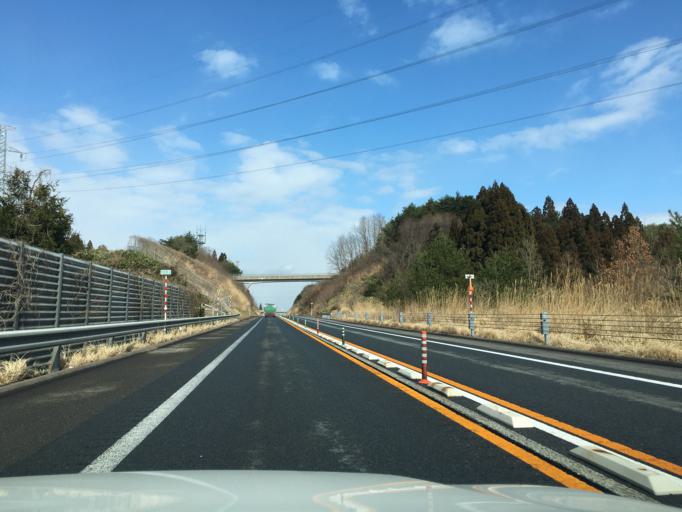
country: JP
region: Akita
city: Akita Shi
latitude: 39.8071
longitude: 140.0948
